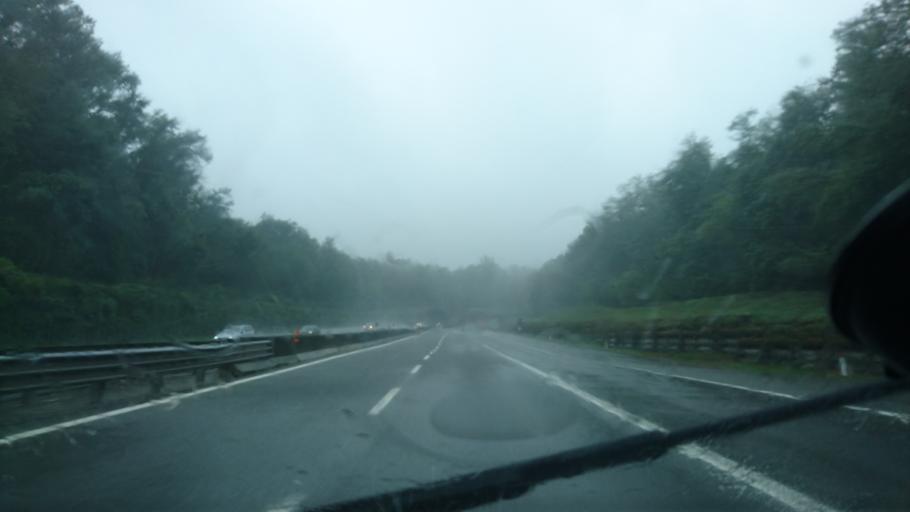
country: IT
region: Piedmont
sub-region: Provincia di Novara
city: Gattico
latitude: 45.7164
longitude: 8.5339
